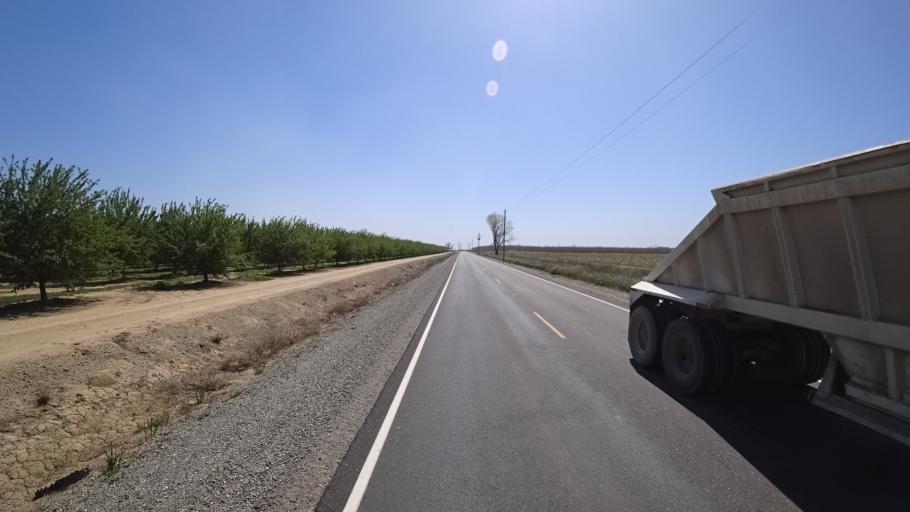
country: US
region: California
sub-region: Glenn County
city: Willows
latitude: 39.6145
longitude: -122.1376
